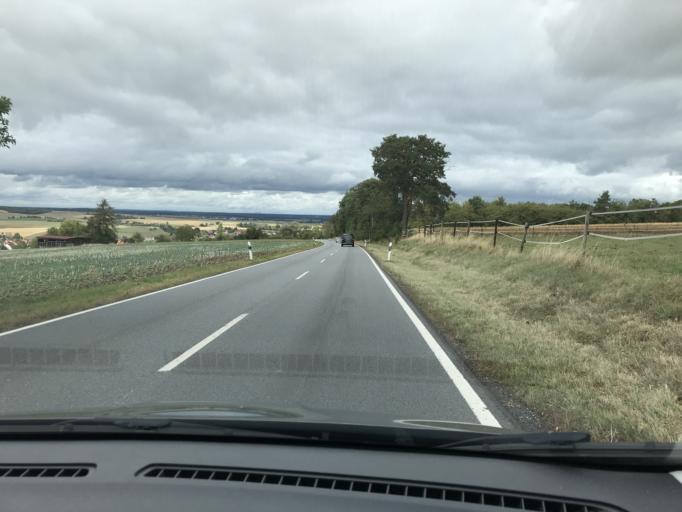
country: DE
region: Bavaria
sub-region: Regierungsbezirk Unterfranken
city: Grossostheim
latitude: 49.9012
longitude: 9.0698
